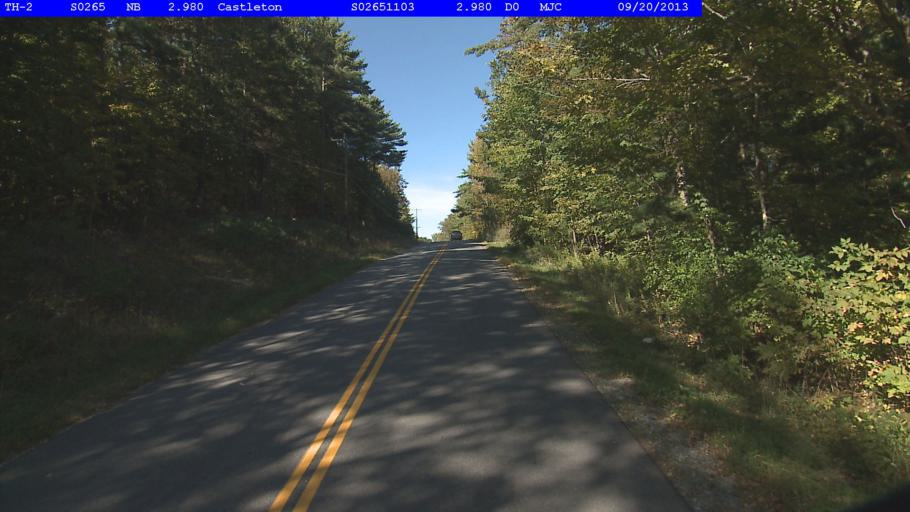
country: US
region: Vermont
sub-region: Rutland County
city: Fair Haven
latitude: 43.6437
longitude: -73.2334
